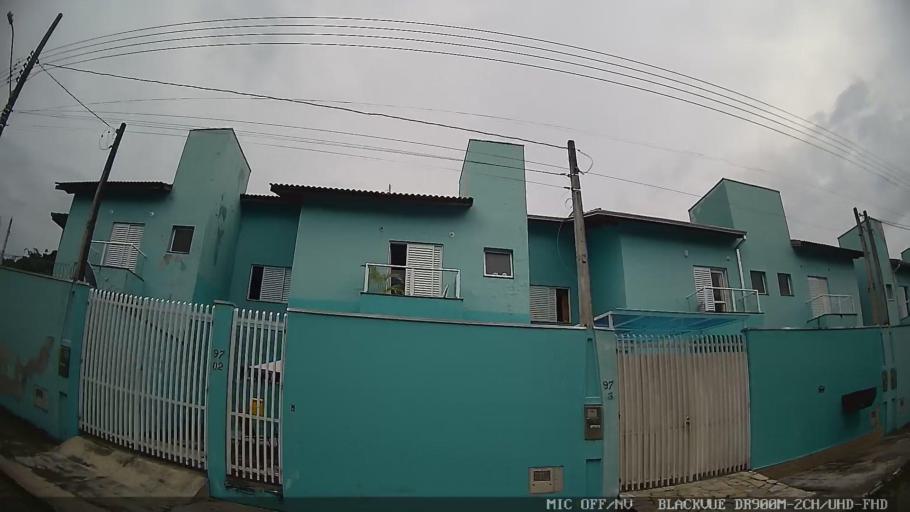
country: BR
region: Sao Paulo
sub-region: Caraguatatuba
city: Caraguatatuba
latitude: -23.6251
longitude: -45.3899
